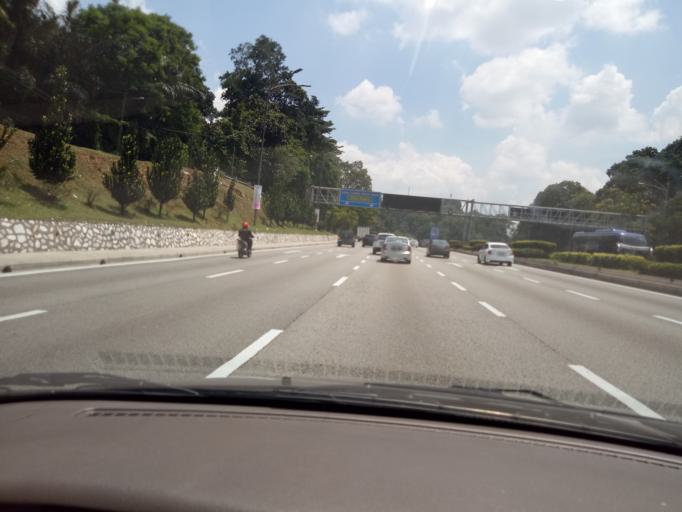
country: MY
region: Kuala Lumpur
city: Kuala Lumpur
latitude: 3.1409
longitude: 101.6802
